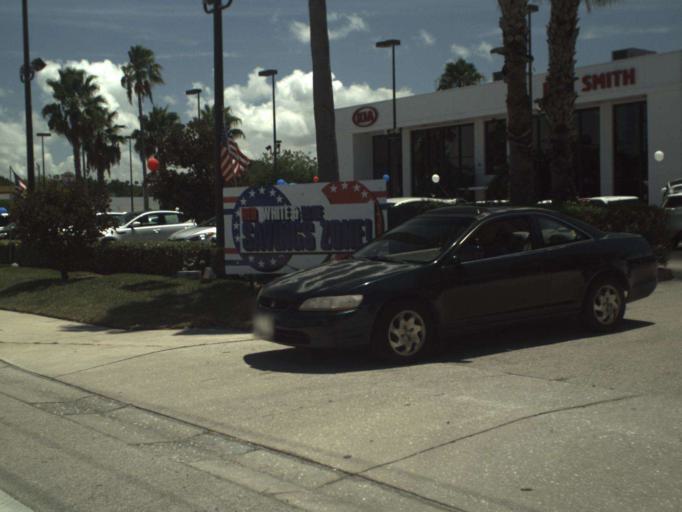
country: US
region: Florida
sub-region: Saint Lucie County
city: White City
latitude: 27.3631
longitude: -80.3260
